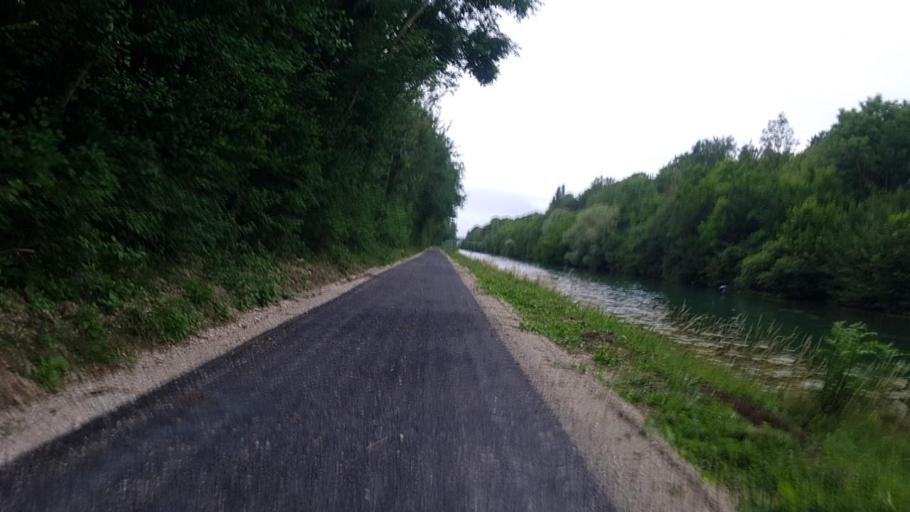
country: FR
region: Champagne-Ardenne
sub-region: Departement de la Marne
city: Sarry
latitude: 48.8395
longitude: 4.5041
